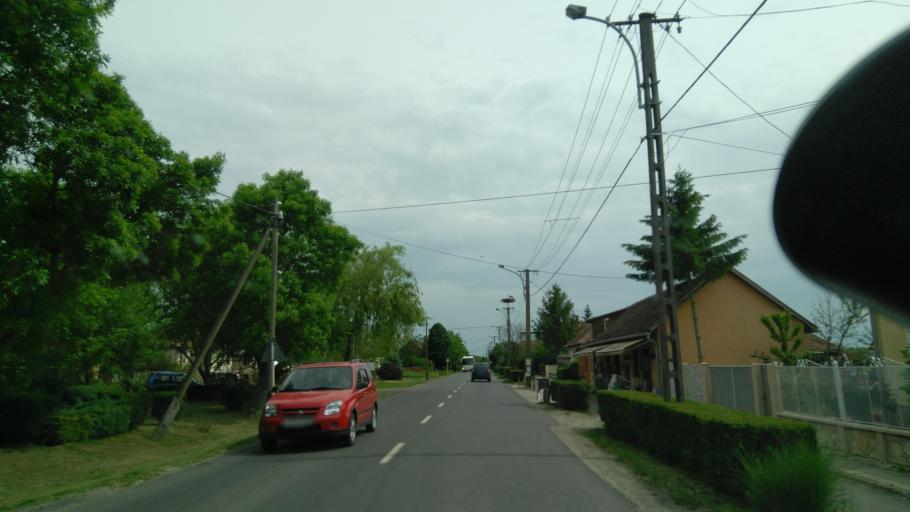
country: HU
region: Bekes
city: Sarkad
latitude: 46.8049
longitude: 21.3825
